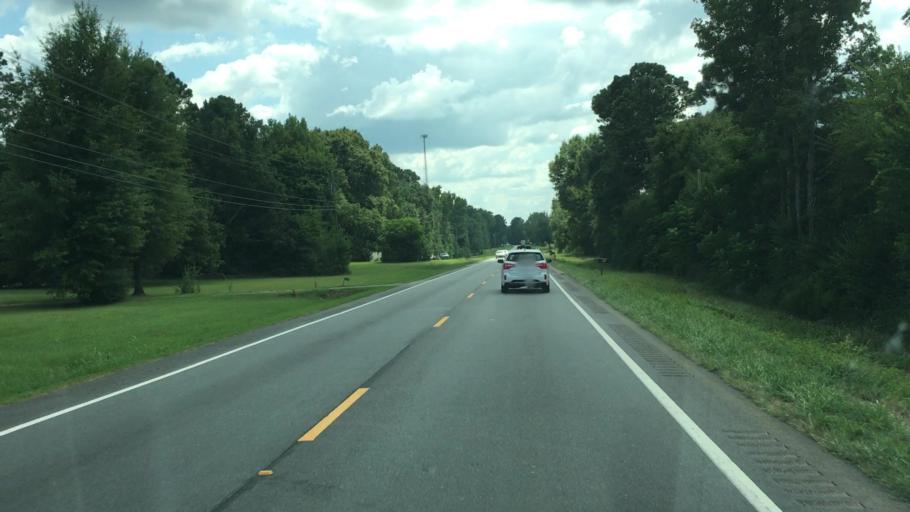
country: US
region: Georgia
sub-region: Putnam County
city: Eatonton
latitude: 33.3868
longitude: -83.3747
